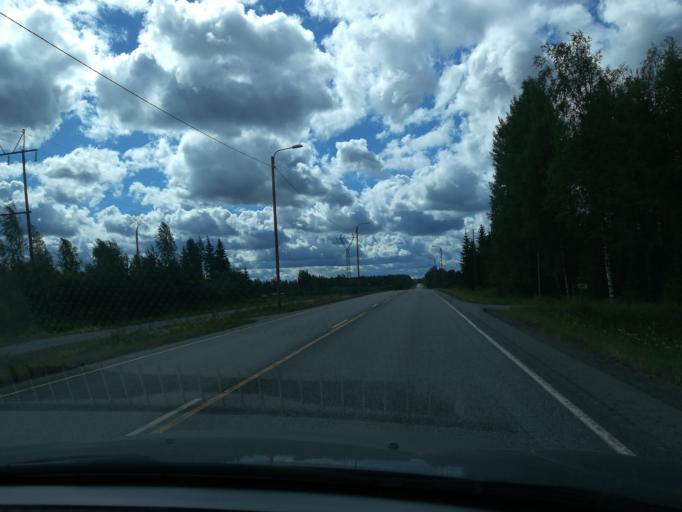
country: FI
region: Southern Savonia
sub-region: Mikkeli
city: Ristiina
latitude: 61.4929
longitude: 27.2433
